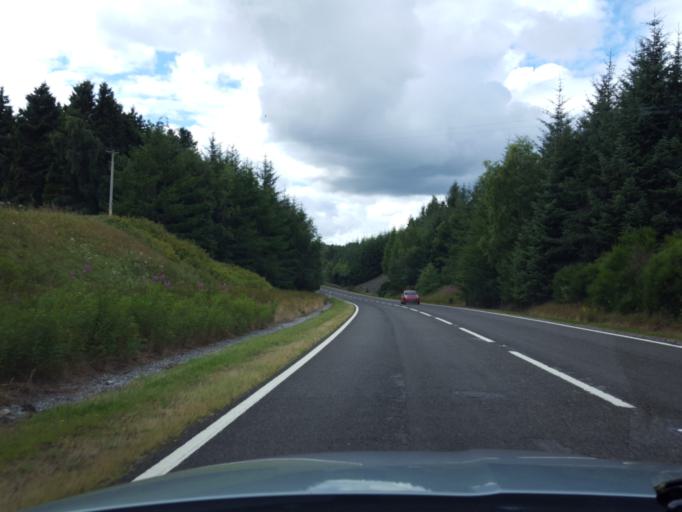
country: GB
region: Scotland
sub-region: Highland
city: Grantown on Spey
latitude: 57.3032
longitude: -3.6581
